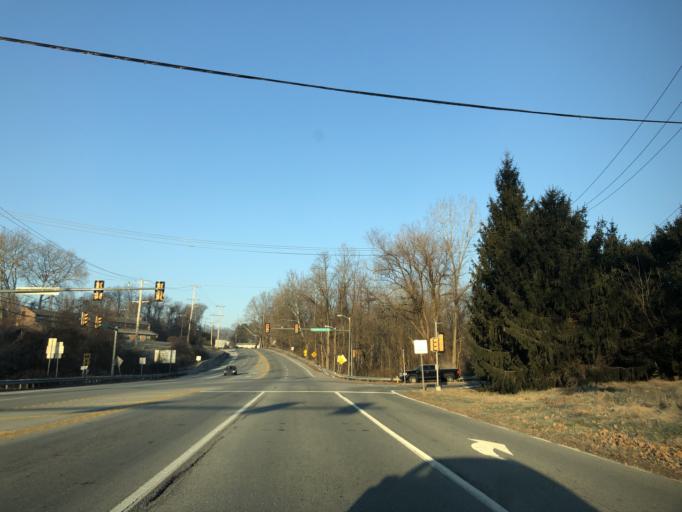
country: US
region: Pennsylvania
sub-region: Chester County
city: West Chester
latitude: 39.9665
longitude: -75.6335
